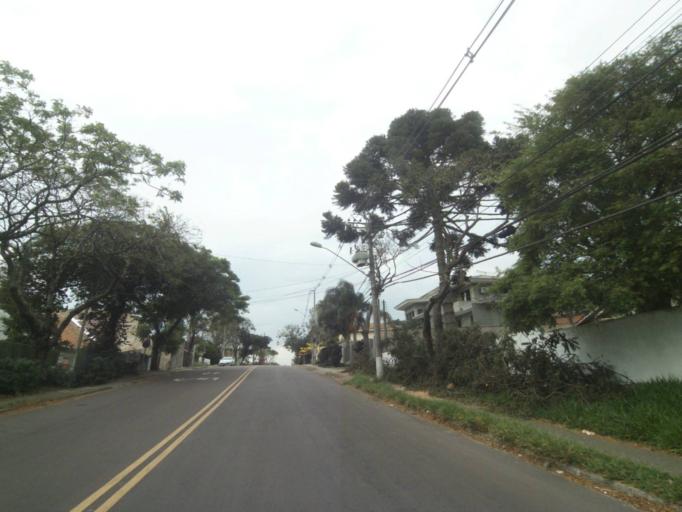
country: BR
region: Parana
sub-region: Pinhais
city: Pinhais
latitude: -25.4825
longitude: -49.2158
